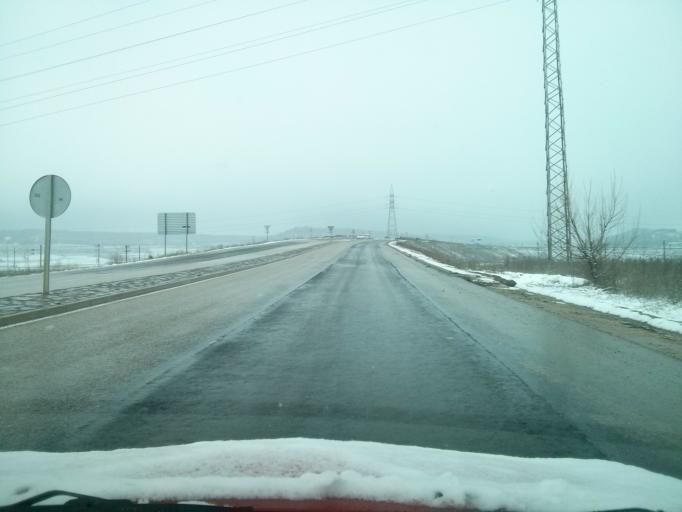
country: ES
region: Castille and Leon
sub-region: Provincia de Burgos
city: Burgos
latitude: 42.3710
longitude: -3.6576
